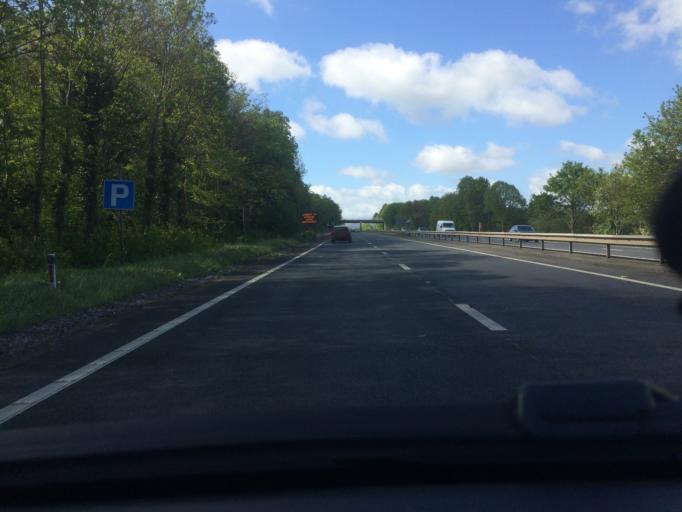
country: GB
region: Wales
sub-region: Wrexham
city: Wrexham
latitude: 53.0672
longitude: -2.9959
